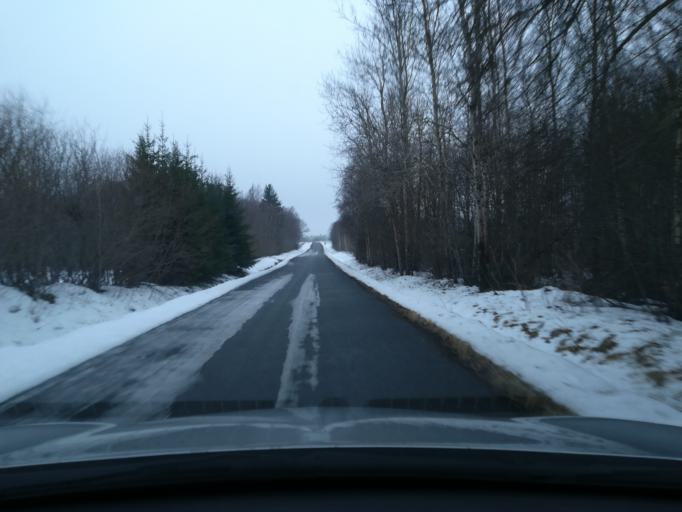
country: EE
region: Harju
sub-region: Raasiku vald
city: Raasiku
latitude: 59.3409
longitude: 25.2435
